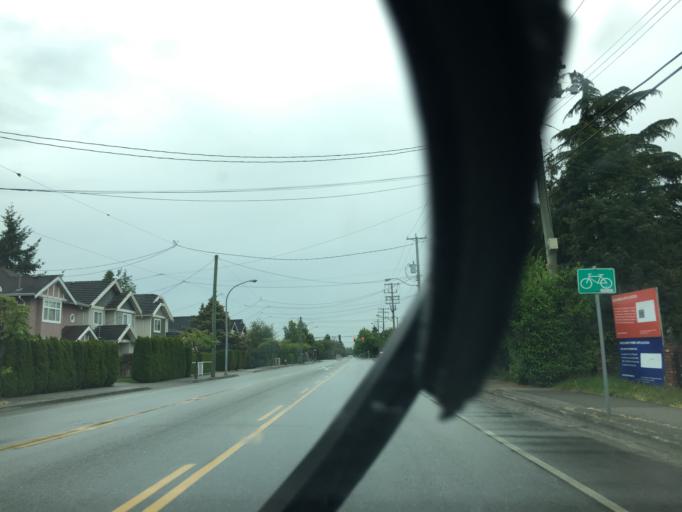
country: CA
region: British Columbia
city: Richmond
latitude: 49.1408
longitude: -123.1168
